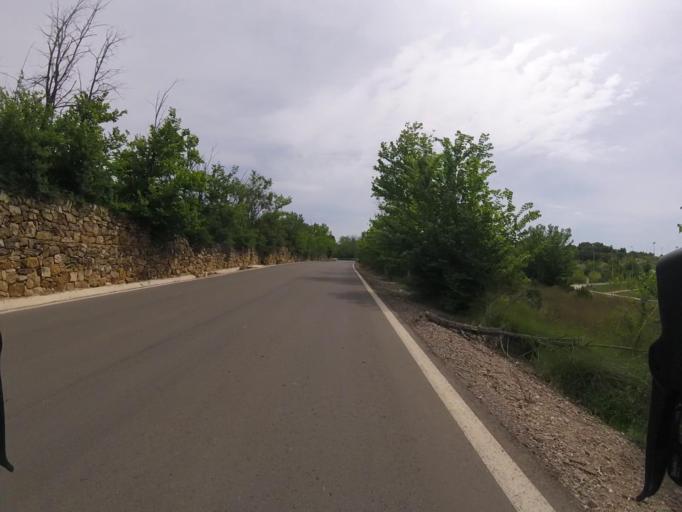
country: ES
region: Valencia
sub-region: Provincia de Castello
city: Cabanes
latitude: 40.1537
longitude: 0.0502
